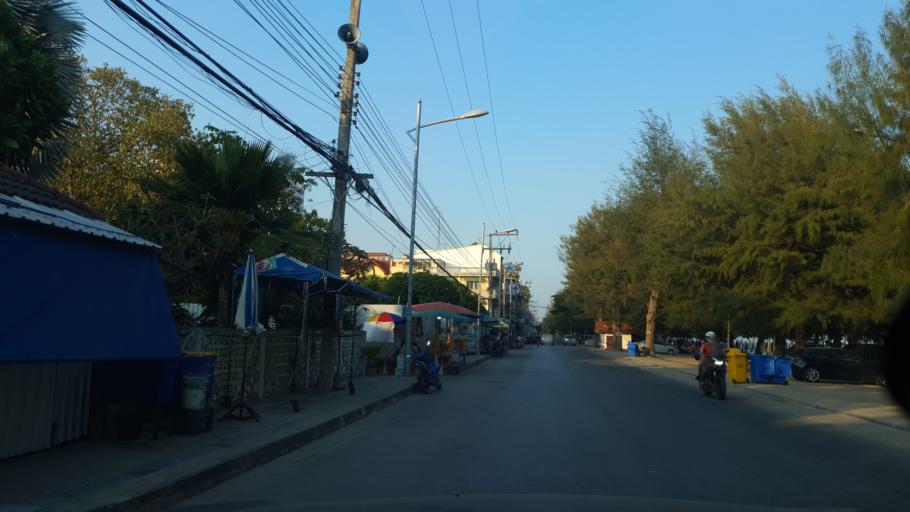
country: TH
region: Phetchaburi
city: Cha-am
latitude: 12.7986
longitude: 99.9852
